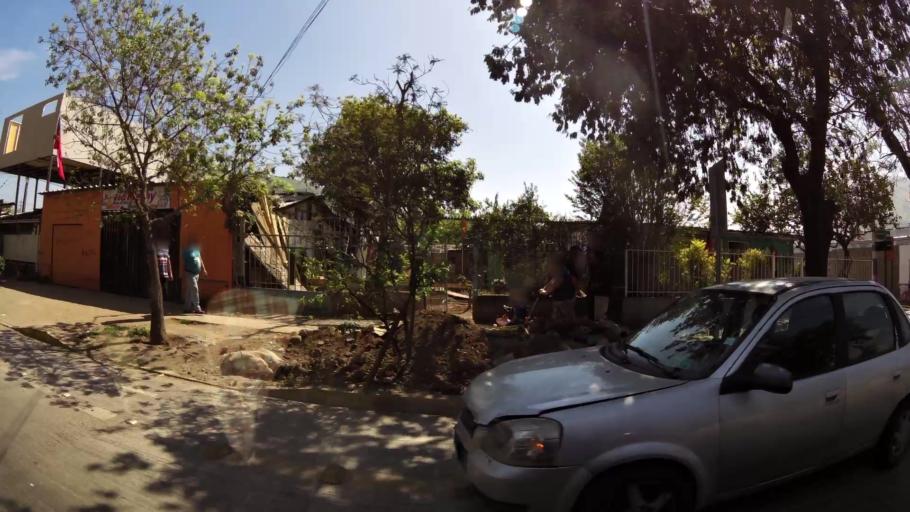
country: CL
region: Santiago Metropolitan
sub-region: Provincia de Santiago
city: Lo Prado
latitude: -33.4019
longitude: -70.7283
